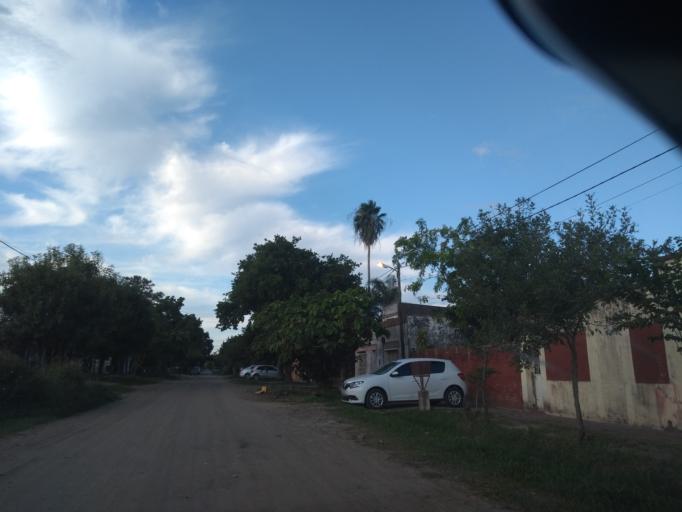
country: AR
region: Chaco
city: Barranqueras
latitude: -27.4876
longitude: -58.9343
